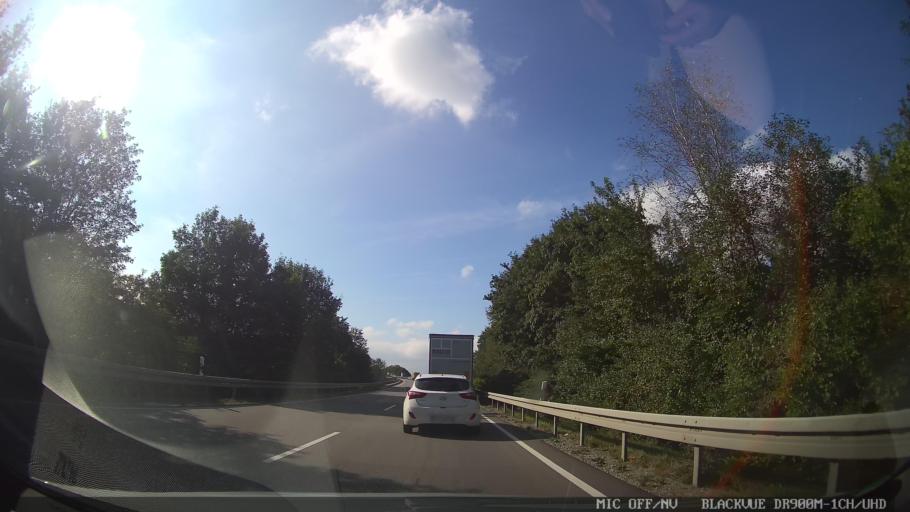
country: DE
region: Baden-Wuerttemberg
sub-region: Freiburg Region
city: Rottweil
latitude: 48.1401
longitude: 8.6511
